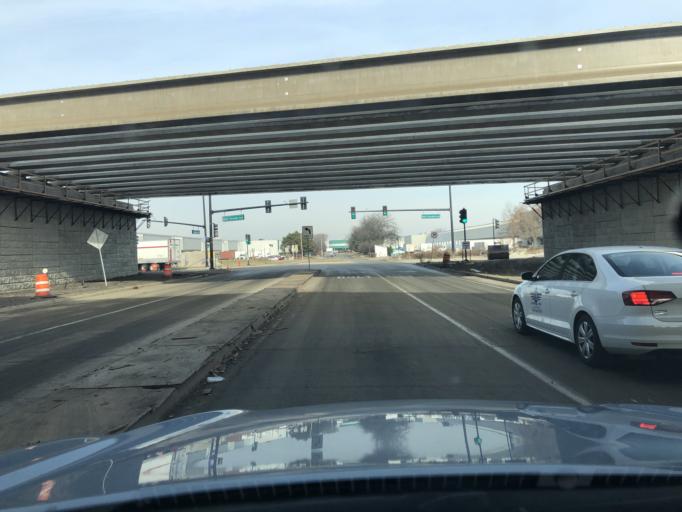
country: US
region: Illinois
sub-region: Cook County
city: Elk Grove Village
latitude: 41.9815
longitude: -87.9527
